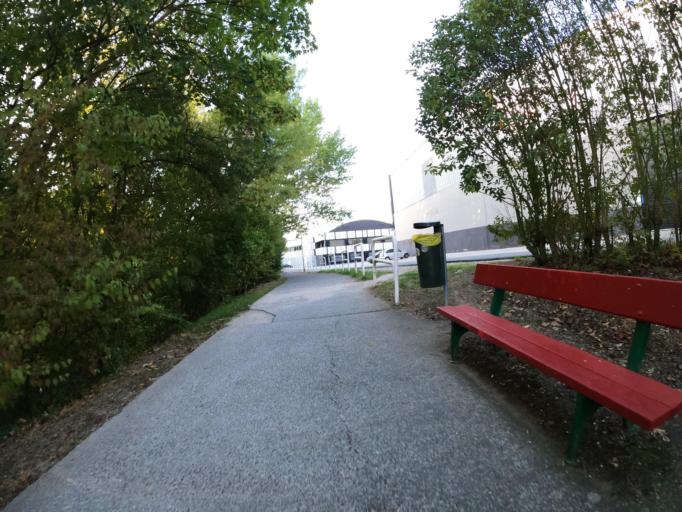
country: ES
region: Navarre
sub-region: Provincia de Navarra
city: Baranain
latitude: 42.8156
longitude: -1.6829
